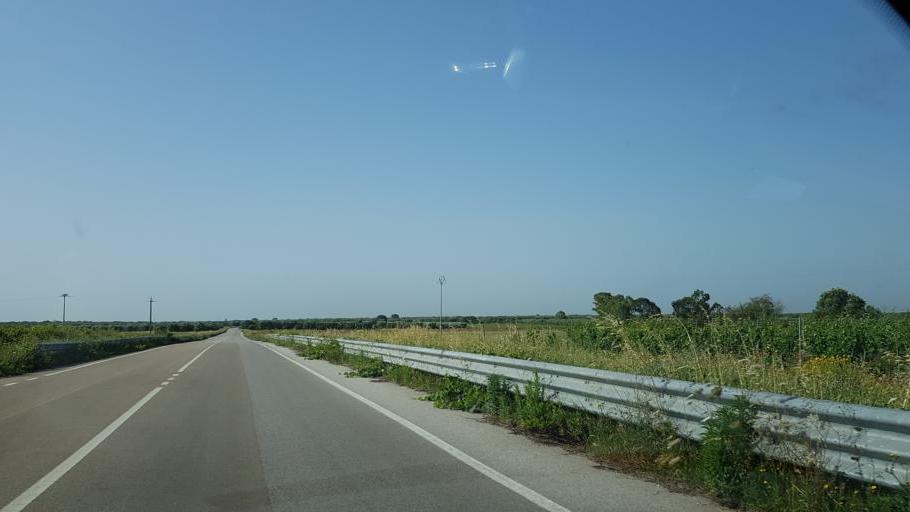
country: IT
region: Apulia
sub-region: Provincia di Brindisi
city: San Pancrazio Salentino
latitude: 40.4810
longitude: 17.8357
